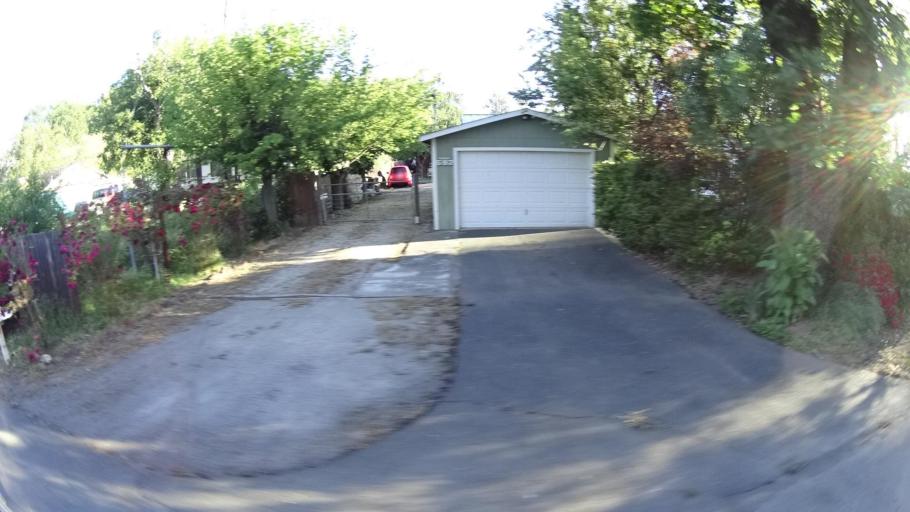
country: US
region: California
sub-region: Lake County
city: Upper Lake
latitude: 39.1708
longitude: -122.9040
